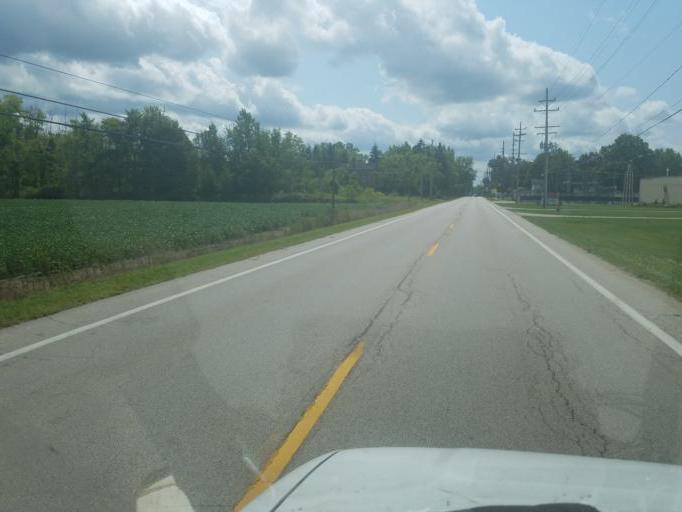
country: US
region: Ohio
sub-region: Ashtabula County
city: Roaming Shores
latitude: 41.6677
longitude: -80.8582
